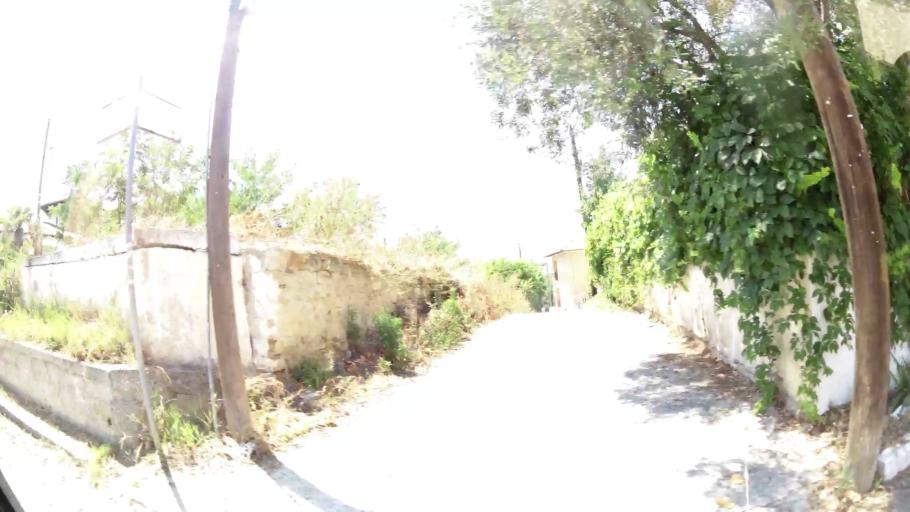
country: GR
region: Central Macedonia
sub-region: Nomos Thessalonikis
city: Trilofos
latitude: 40.4676
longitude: 22.9661
